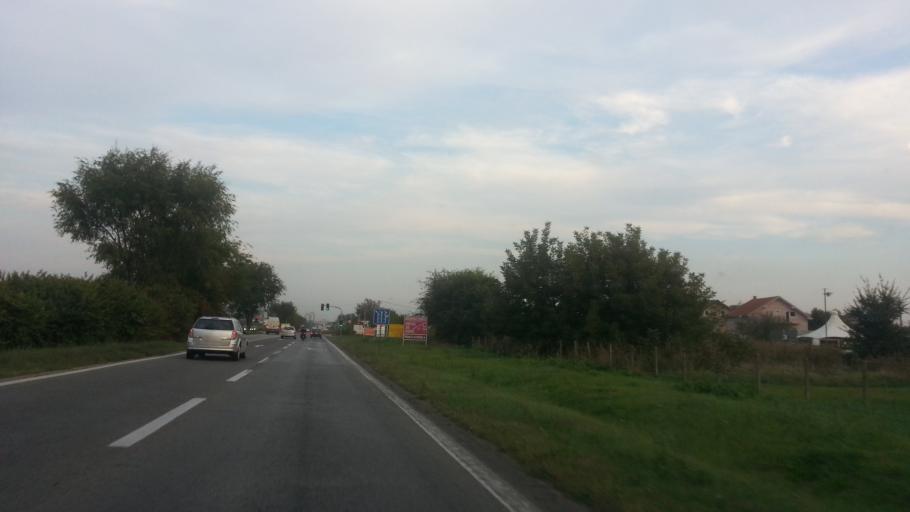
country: RS
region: Central Serbia
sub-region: Belgrade
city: Zemun
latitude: 44.8621
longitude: 20.3514
